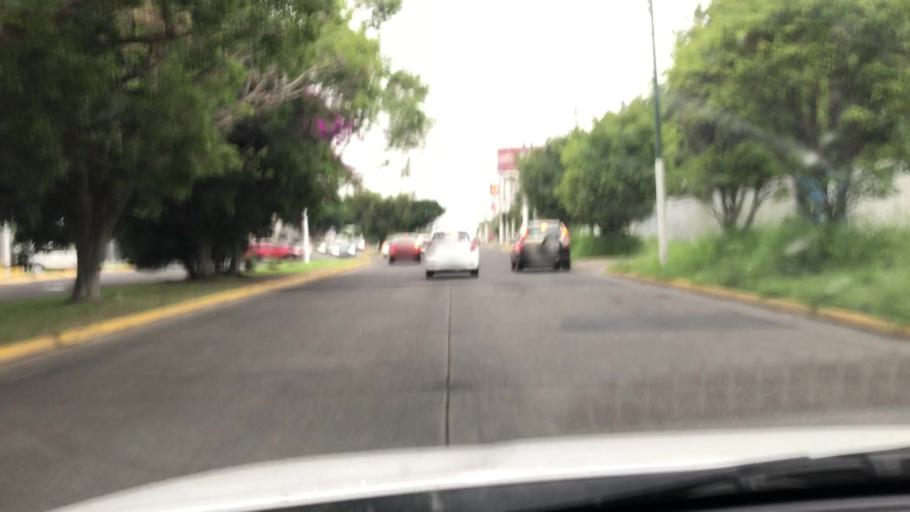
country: MX
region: Jalisco
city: Guadalajara
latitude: 20.6547
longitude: -103.4245
